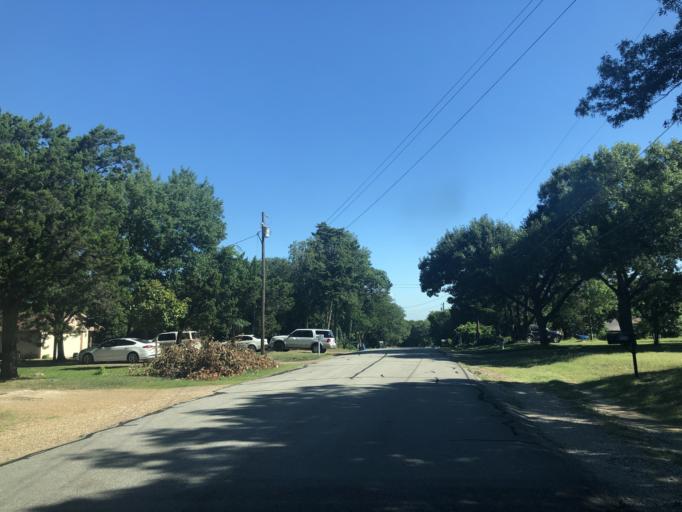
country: US
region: Texas
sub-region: Dallas County
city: Duncanville
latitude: 32.6590
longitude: -96.9391
